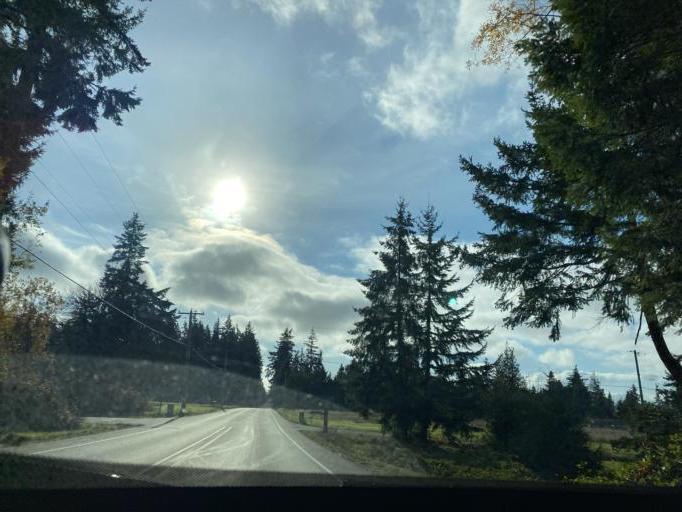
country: US
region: Washington
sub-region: Island County
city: Freeland
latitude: 47.9936
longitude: -122.4616
